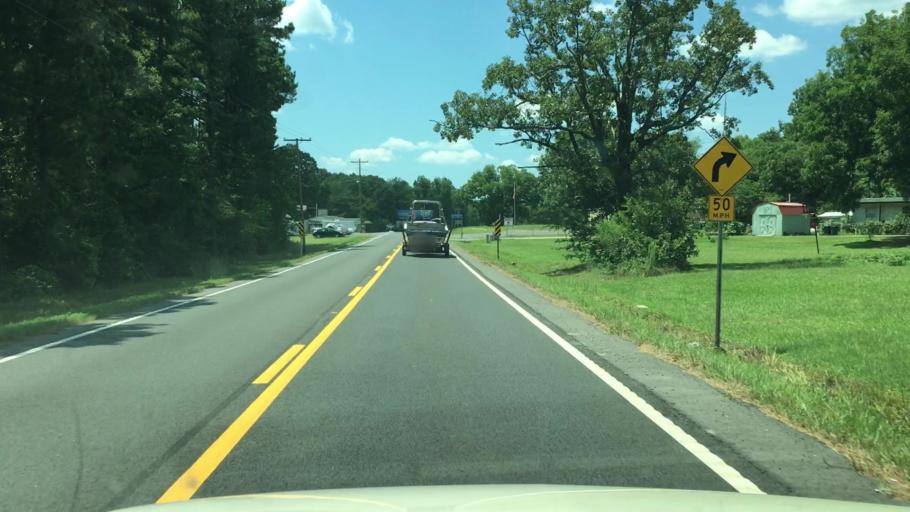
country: US
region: Arkansas
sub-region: Garland County
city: Lake Hamilton
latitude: 34.2676
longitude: -93.1419
